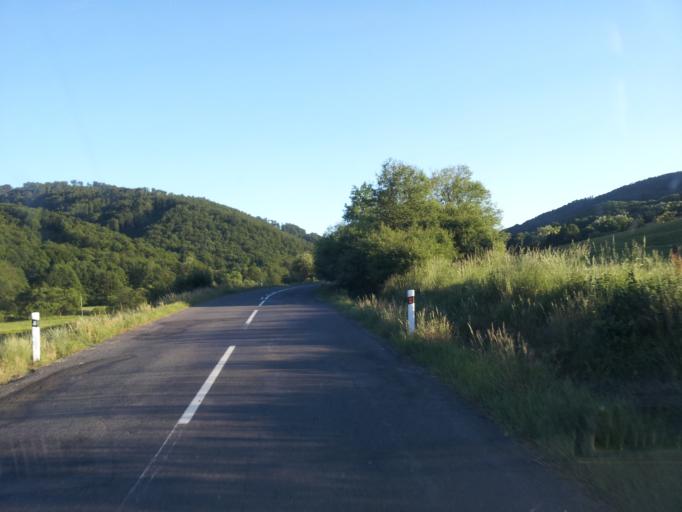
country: SK
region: Banskobystricky
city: Svaety Anton
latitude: 48.4023
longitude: 18.9394
